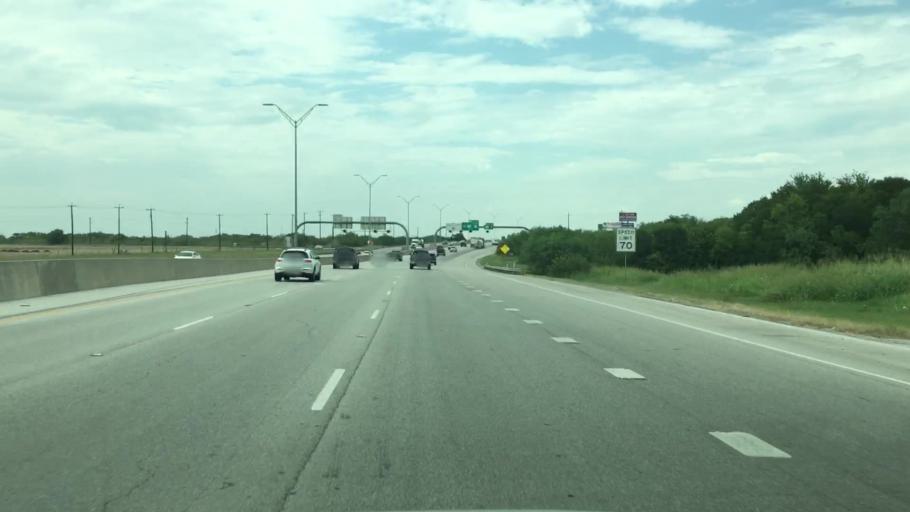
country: US
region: Texas
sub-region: Bexar County
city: Elmendorf
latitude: 29.3113
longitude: -98.4030
